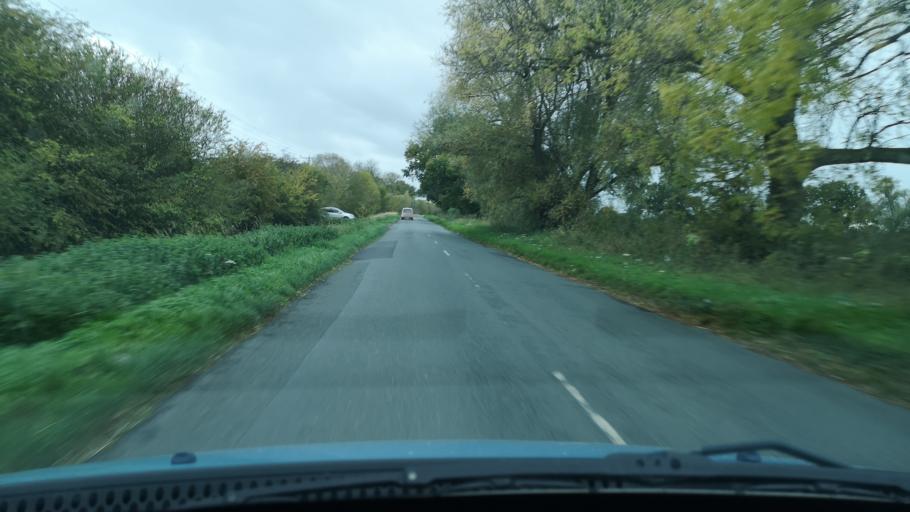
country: GB
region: England
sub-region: Doncaster
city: Hatfield
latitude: 53.6170
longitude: -0.9933
